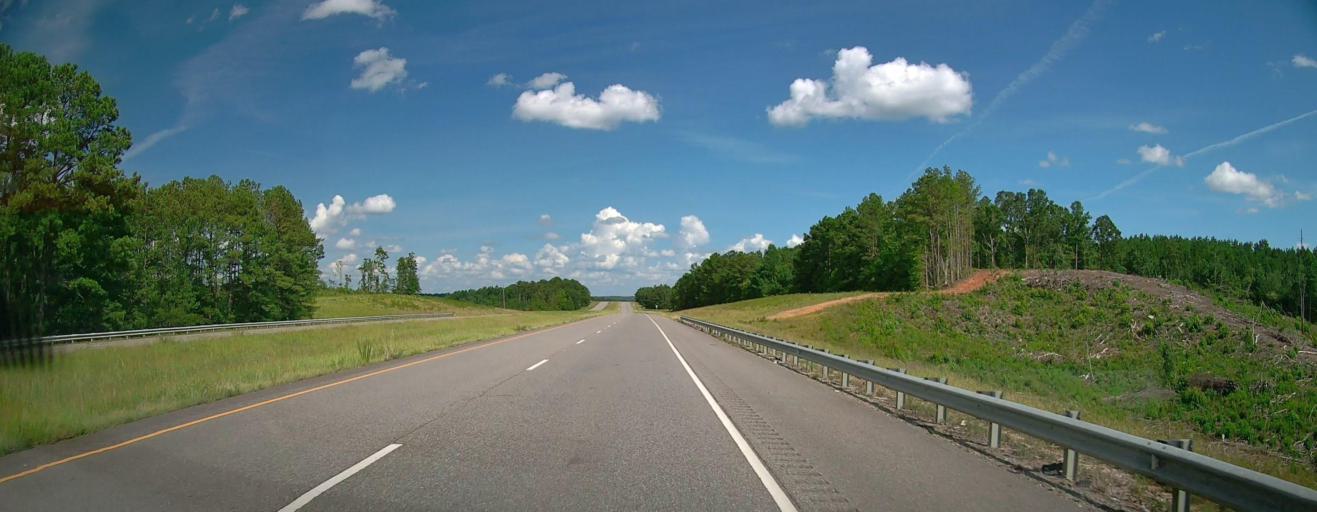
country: US
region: Alabama
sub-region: Pickens County
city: Reform
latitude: 33.3954
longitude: -88.0546
